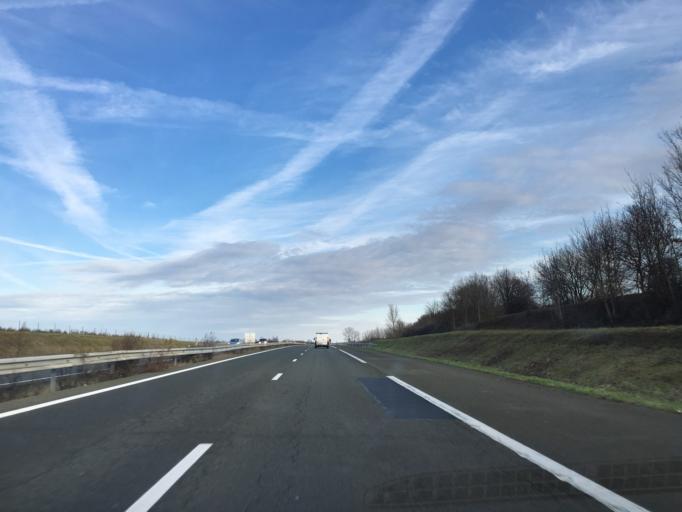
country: FR
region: Picardie
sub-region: Departement de l'Aisne
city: Essomes-sur-Marne
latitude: 49.0628
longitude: 3.3323
